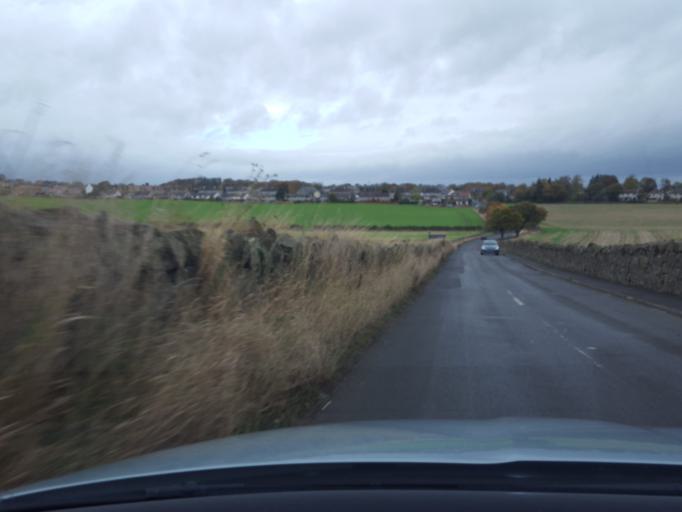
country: GB
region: Scotland
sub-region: Edinburgh
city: Ratho
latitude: 55.9168
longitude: -3.3762
